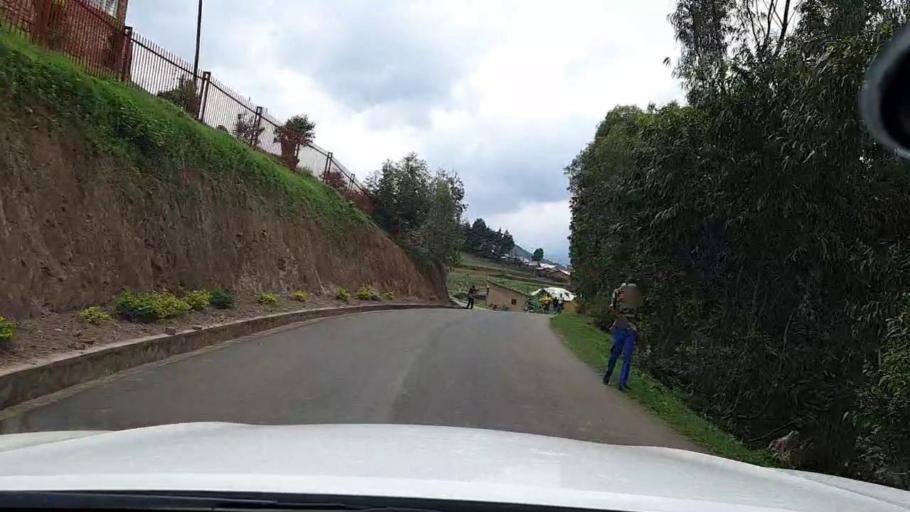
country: RW
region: Western Province
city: Kibuye
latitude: -2.1816
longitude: 29.2921
